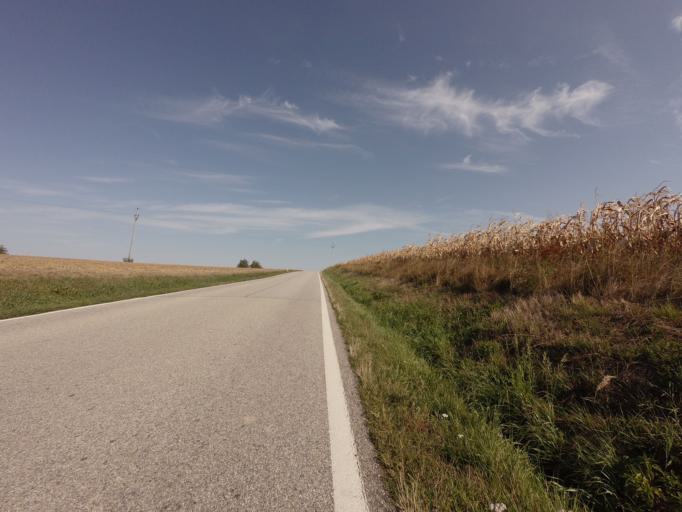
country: CZ
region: Jihocesky
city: Tyn nad Vltavou
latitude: 49.2894
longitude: 14.3924
